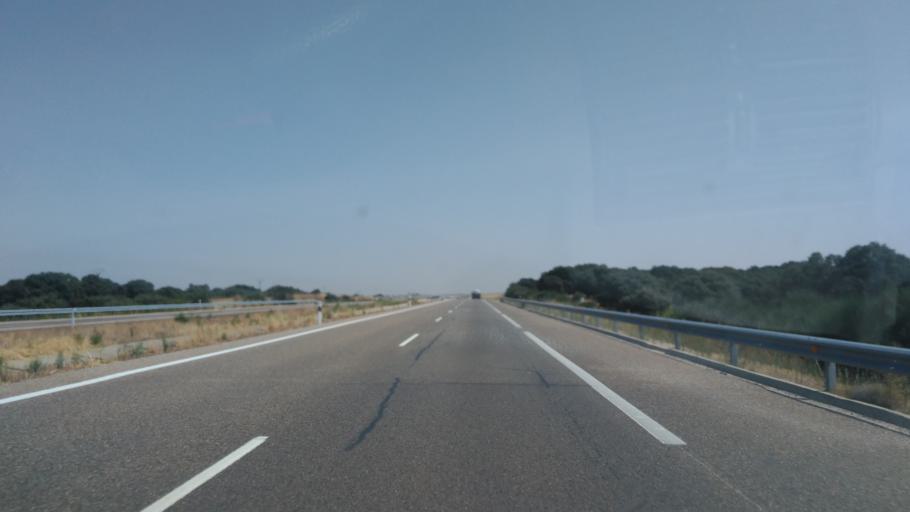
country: ES
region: Castille and Leon
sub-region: Provincia de Salamanca
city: Aldehuela de la Boveda
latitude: 40.8619
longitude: -6.0181
